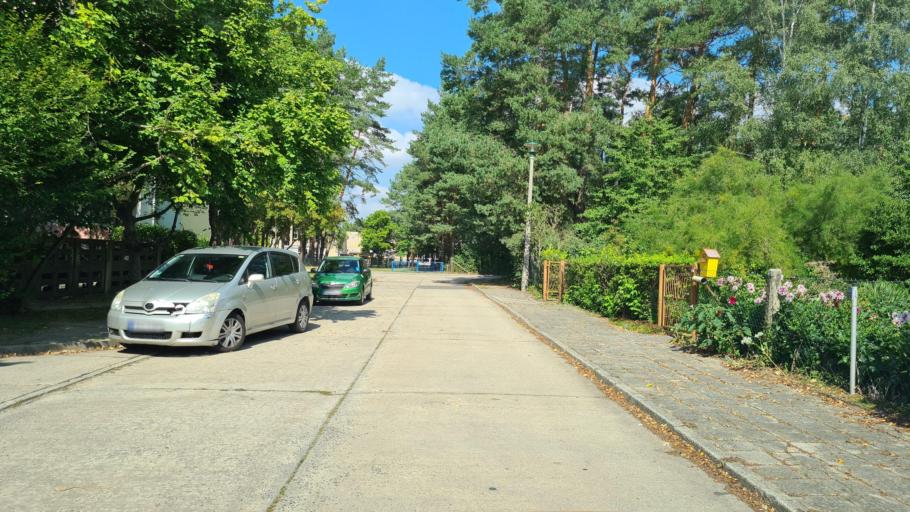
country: DE
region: Brandenburg
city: Sonnewalde
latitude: 51.7777
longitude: 13.6125
